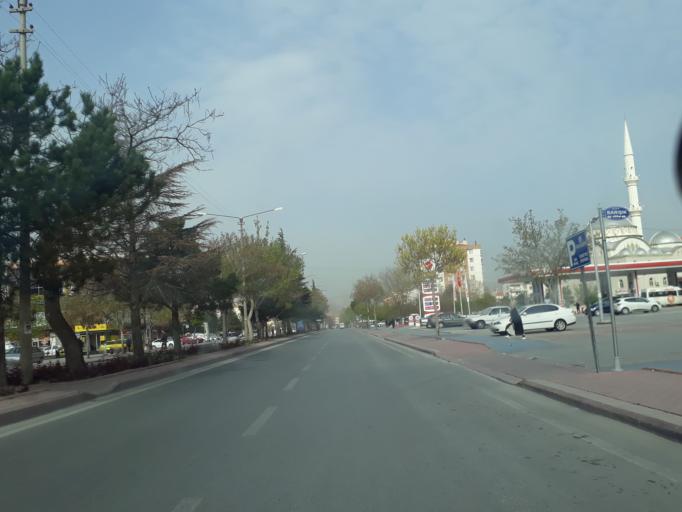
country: TR
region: Konya
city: Selcuklu
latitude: 37.9372
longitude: 32.5025
